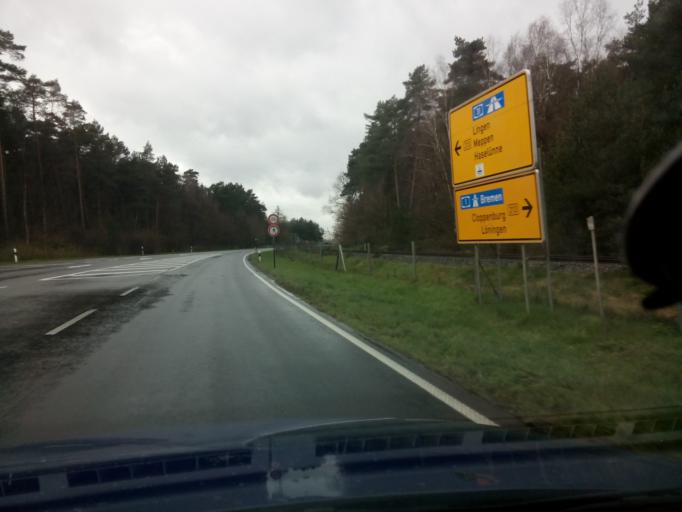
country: DE
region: Lower Saxony
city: Herzlake
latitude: 52.6947
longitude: 7.6209
